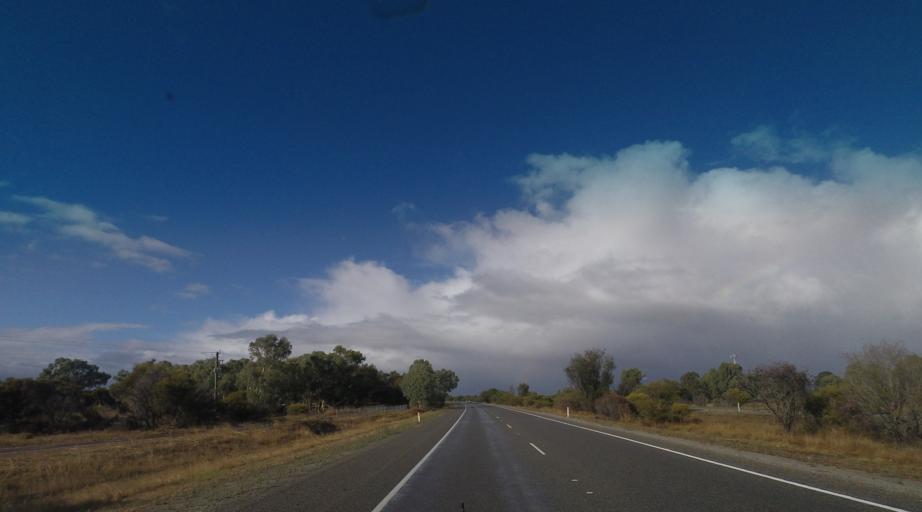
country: AU
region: Western Australia
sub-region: Armadale
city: Brookdale
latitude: -32.1669
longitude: 115.9611
